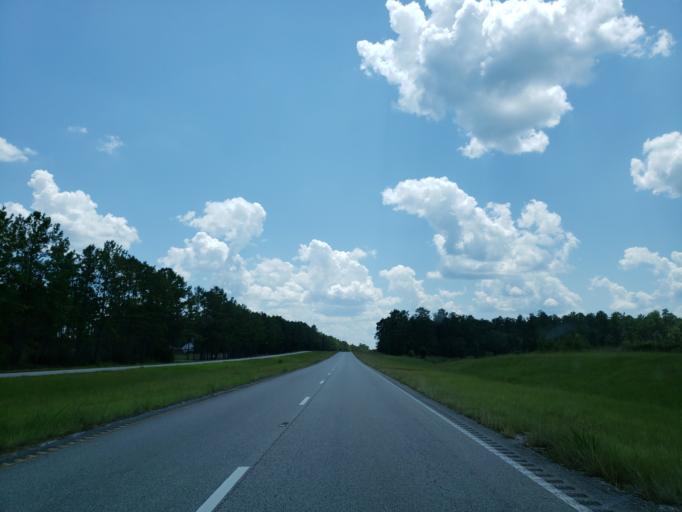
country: US
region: Mississippi
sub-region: Wayne County
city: Belmont
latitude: 31.3761
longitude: -88.4842
